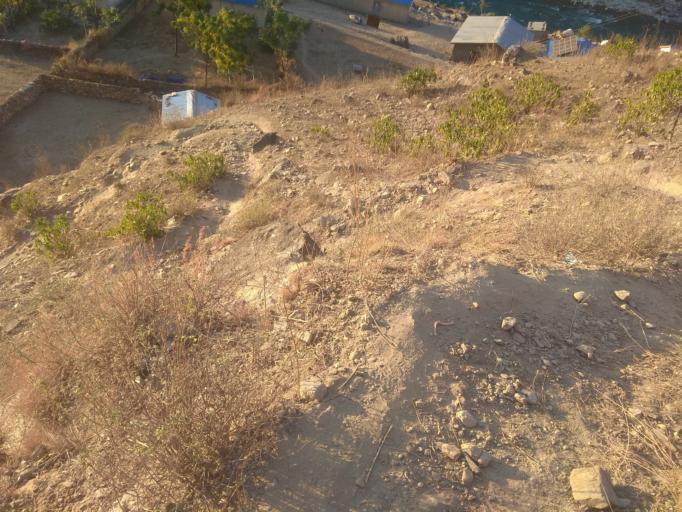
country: NP
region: Mid Western
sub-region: Bheri Zone
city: Dailekh
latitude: 29.2769
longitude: 81.7311
